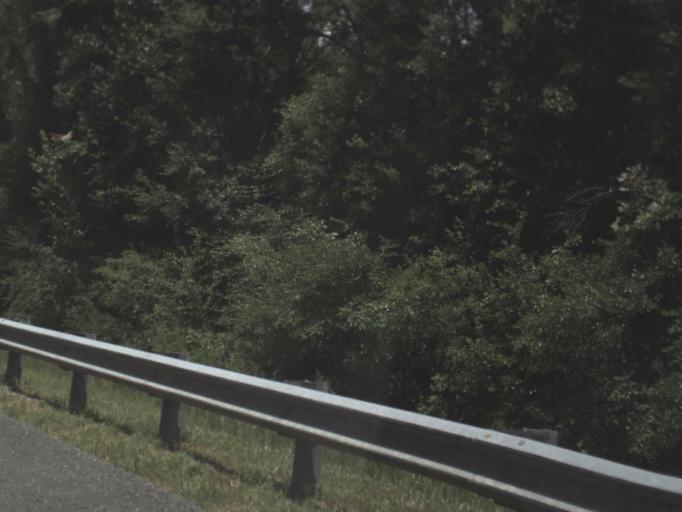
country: US
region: Florida
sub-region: Lafayette County
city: Mayo
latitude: 30.1169
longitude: -83.1701
